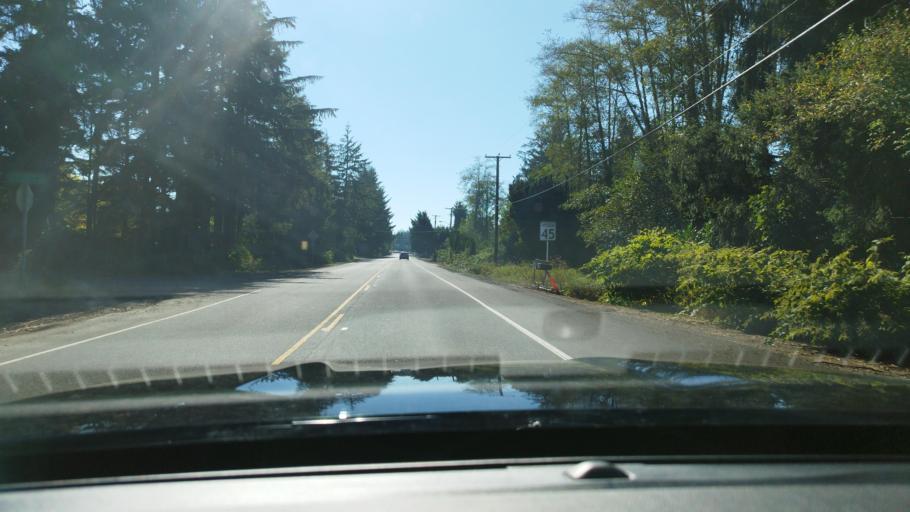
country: US
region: Oregon
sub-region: Clatsop County
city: Warrenton
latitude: 46.1533
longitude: -123.9153
